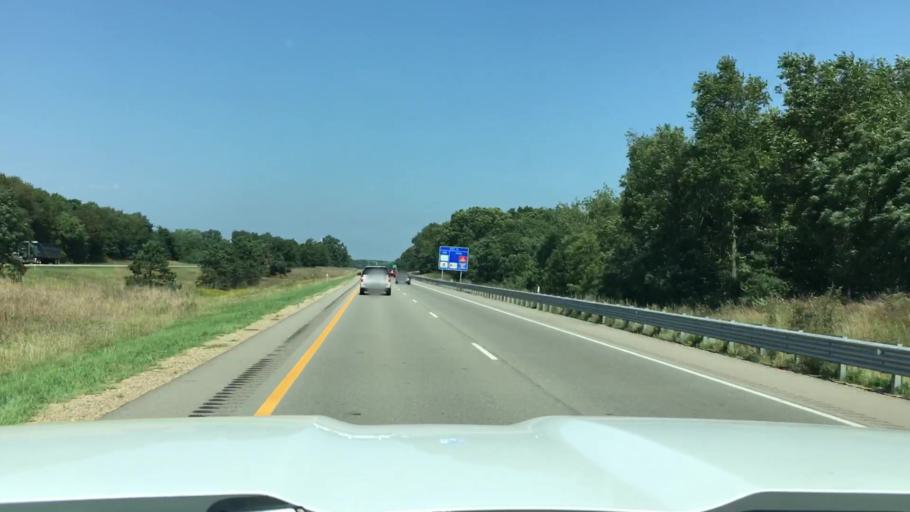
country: US
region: Michigan
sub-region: Kalamazoo County
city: Schoolcraft
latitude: 42.1808
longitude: -85.6455
